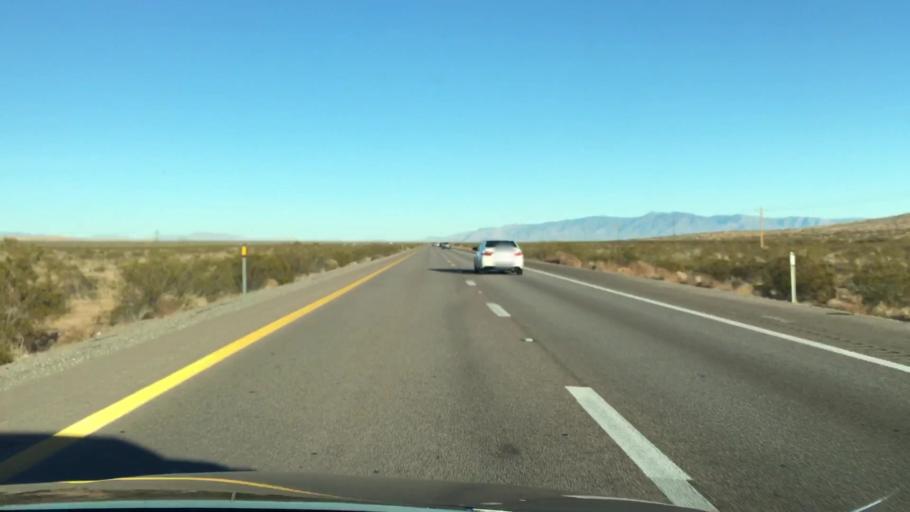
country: US
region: Nevada
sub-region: Clark County
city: Moapa Valley
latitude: 36.7471
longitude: -114.4114
